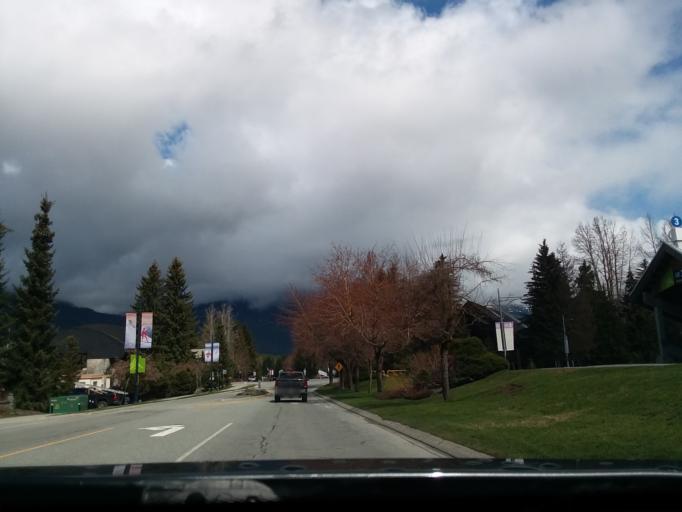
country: CA
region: British Columbia
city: Whistler
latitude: 50.1166
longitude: -122.9535
